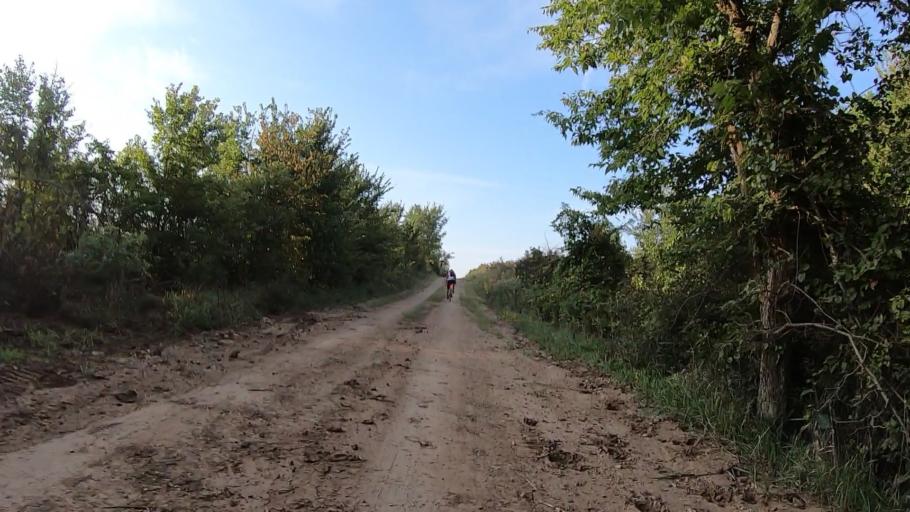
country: US
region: Kansas
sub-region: Marshall County
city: Blue Rapids
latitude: 39.7569
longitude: -96.7506
